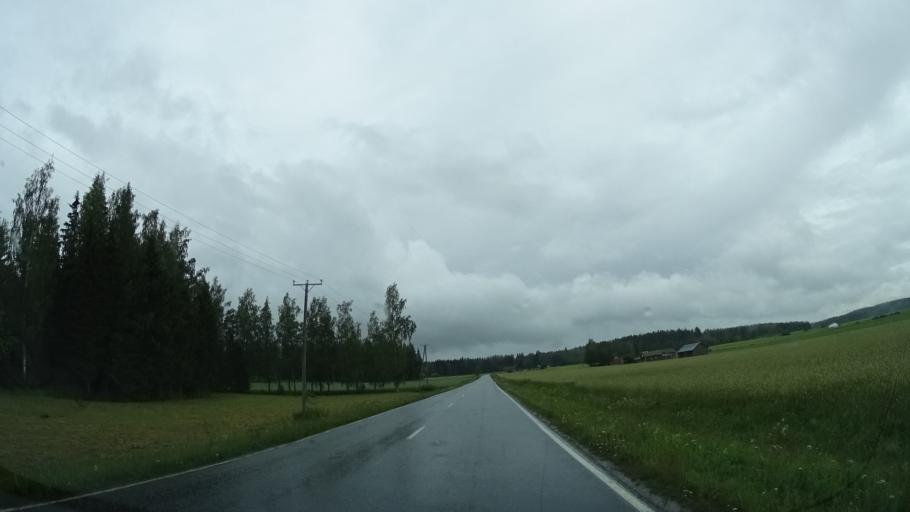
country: FI
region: Haeme
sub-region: Forssa
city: Humppila
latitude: 60.9820
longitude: 23.2533
